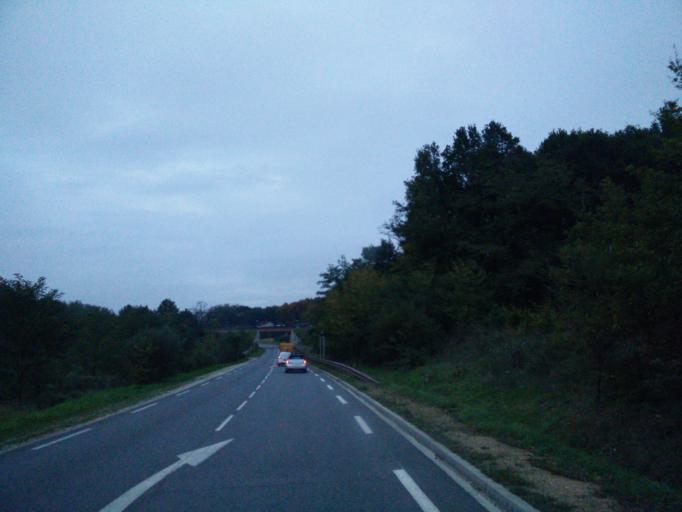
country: FR
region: Aquitaine
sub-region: Departement de la Dordogne
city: Sarlat-la-Caneda
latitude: 44.8797
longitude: 1.2068
